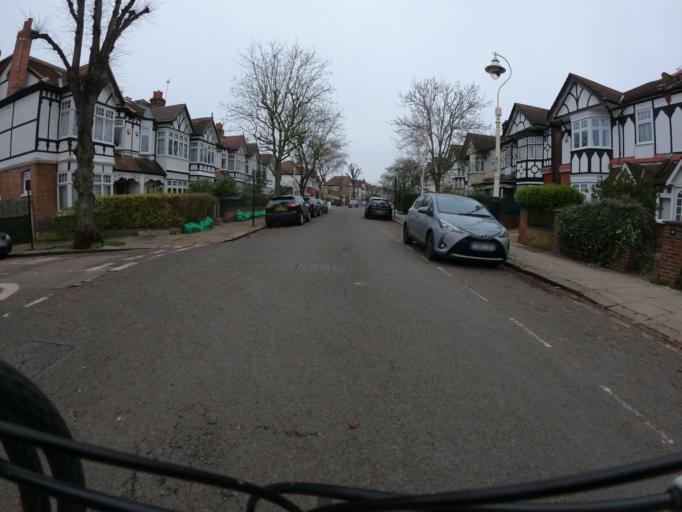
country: GB
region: England
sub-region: Greater London
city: Ealing
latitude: 51.5066
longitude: -0.3155
